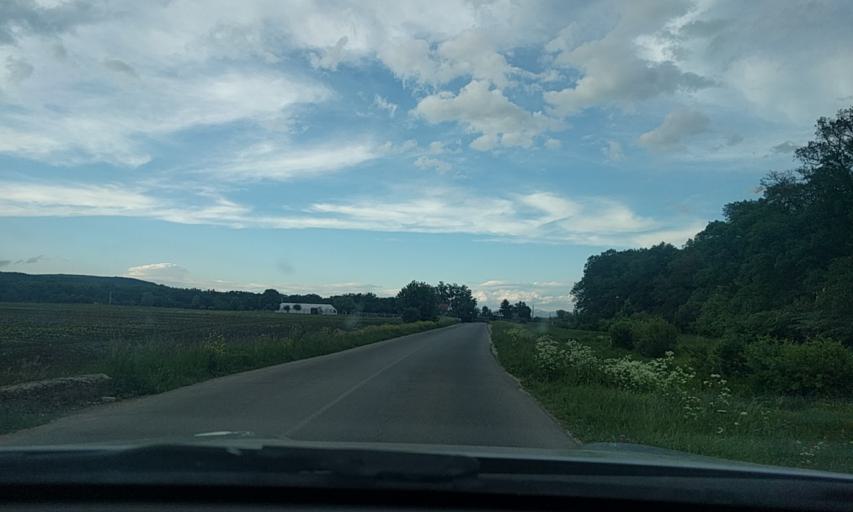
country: RO
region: Brasov
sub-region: Comuna Harman
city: Harman
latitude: 45.7474
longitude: 25.7042
